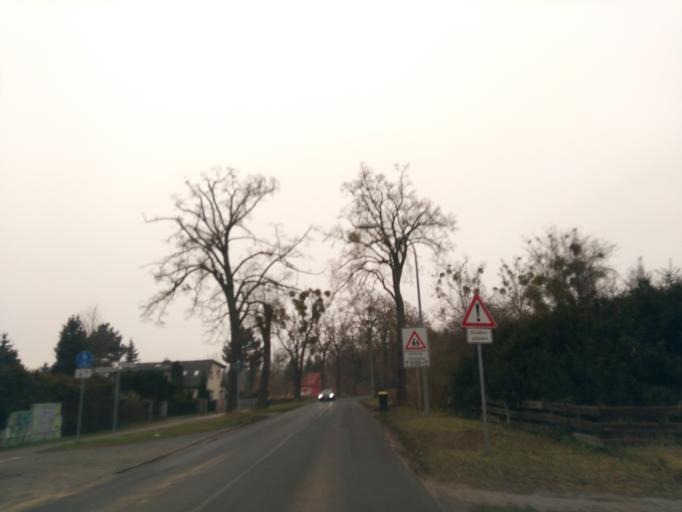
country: DE
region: Brandenburg
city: Dallgow-Doeberitz
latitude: 52.5522
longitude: 13.0556
